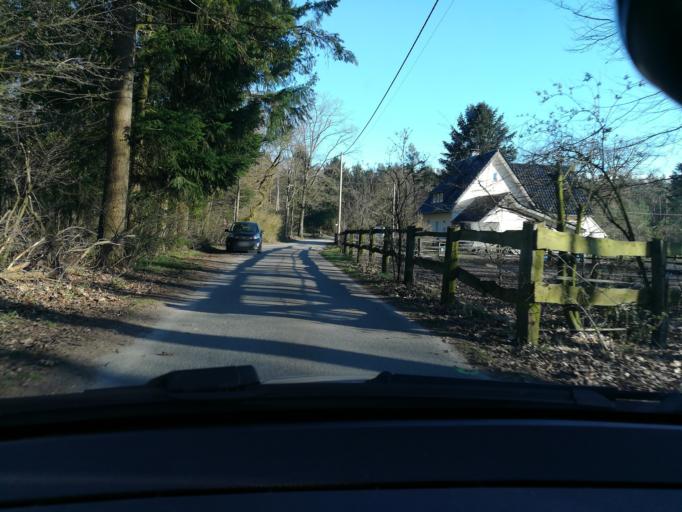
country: DE
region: North Rhine-Westphalia
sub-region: Regierungsbezirk Detmold
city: Oerlinghausen
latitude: 51.9479
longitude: 8.6036
